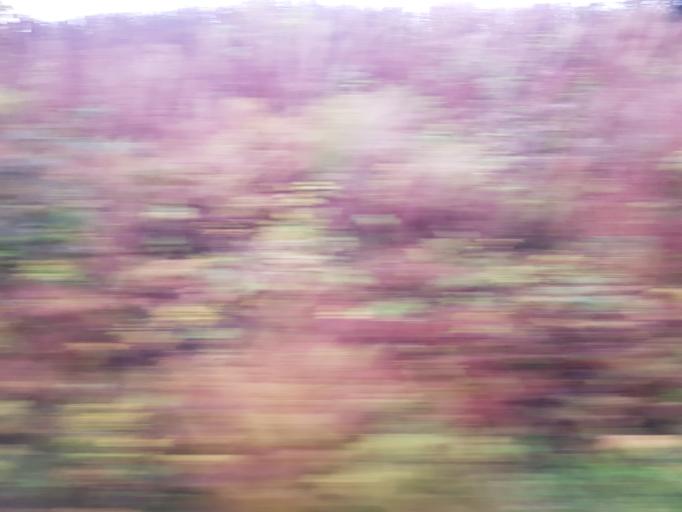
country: NO
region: Sor-Trondelag
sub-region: Melhus
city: Melhus
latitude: 63.2207
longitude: 10.2851
